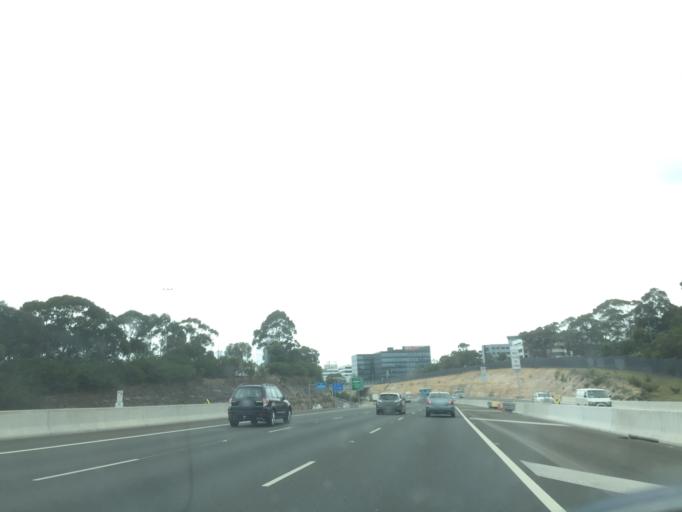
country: AU
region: New South Wales
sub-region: Ryde
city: Macquarie Park
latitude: -33.7696
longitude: 151.1163
